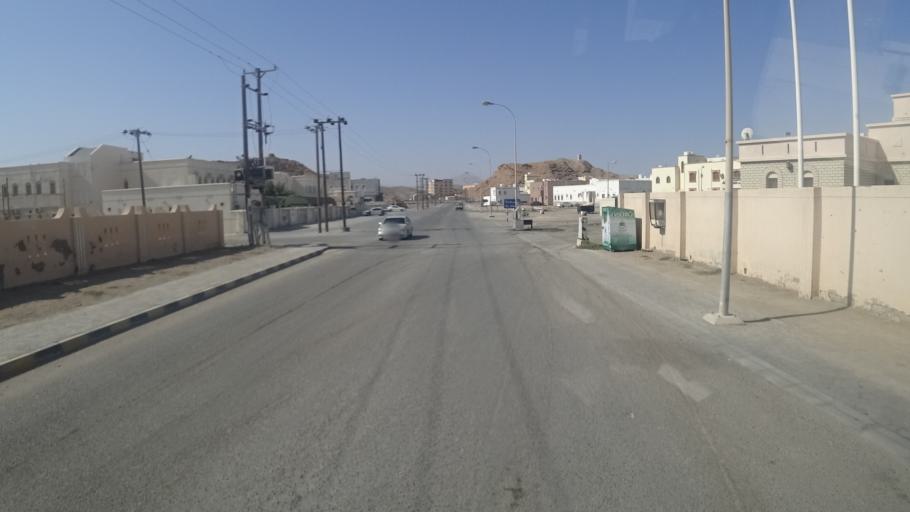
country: OM
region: Ash Sharqiyah
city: Sur
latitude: 22.5659
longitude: 59.5449
